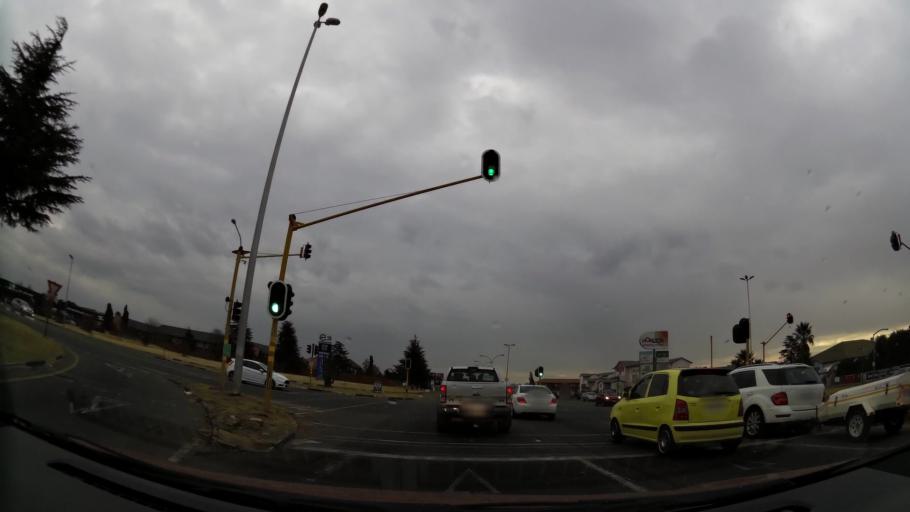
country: ZA
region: Gauteng
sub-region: City of Johannesburg Metropolitan Municipality
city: Roodepoort
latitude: -26.1409
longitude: 27.8698
